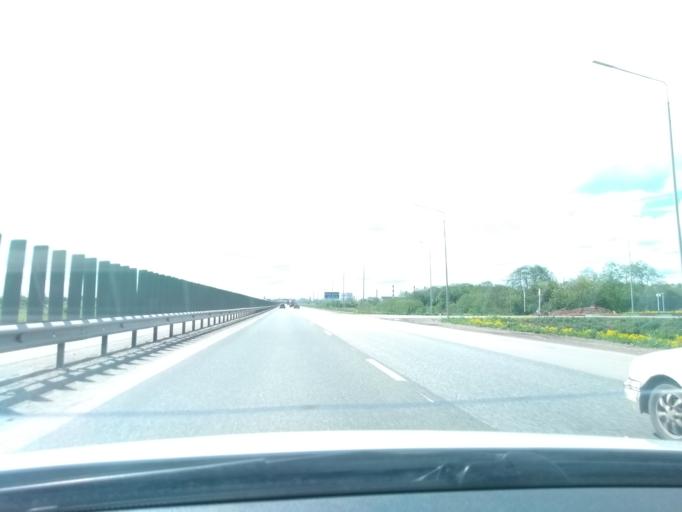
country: RU
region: Perm
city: Froly
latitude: 57.9320
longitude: 56.2028
